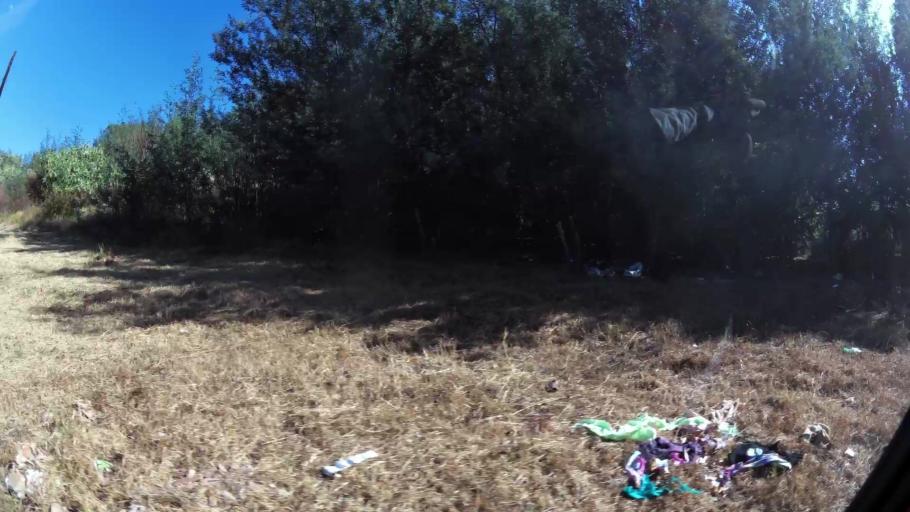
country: ZA
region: Gauteng
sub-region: City of Johannesburg Metropolitan Municipality
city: Roodepoort
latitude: -26.1192
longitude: 27.8680
